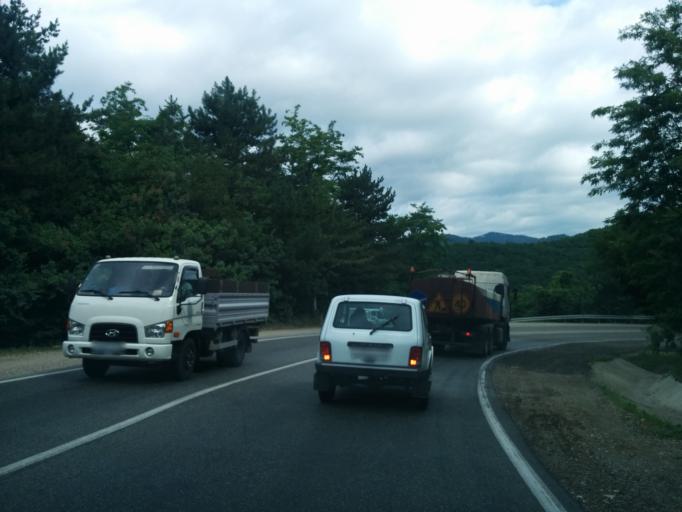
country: RU
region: Krasnodarskiy
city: Agoy
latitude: 44.1396
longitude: 39.0544
